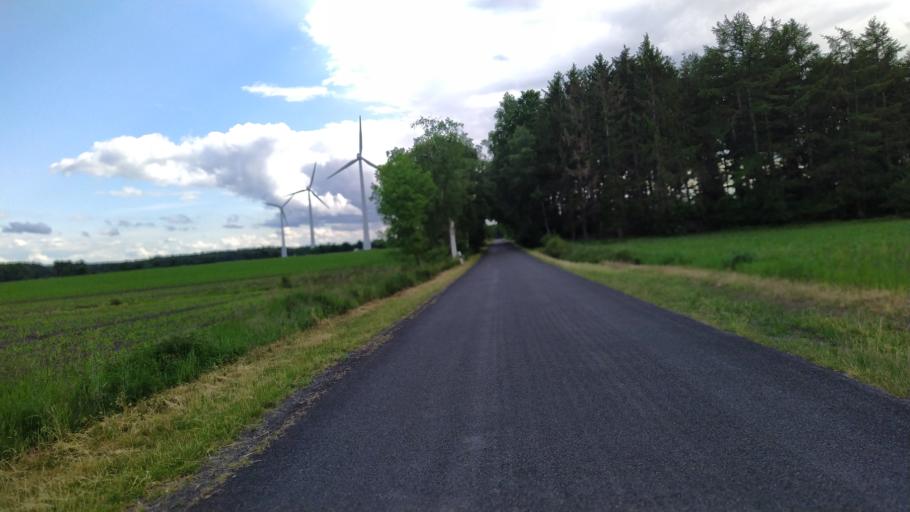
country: DE
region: Lower Saxony
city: Sandbostel
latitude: 53.4286
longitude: 9.1694
